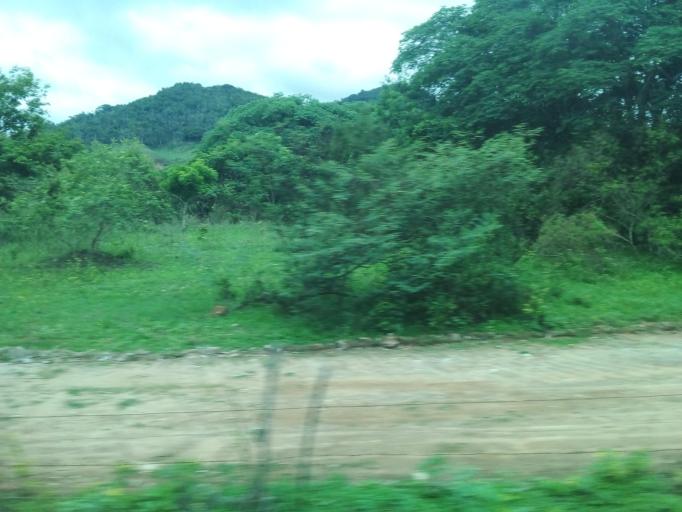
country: BR
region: Minas Gerais
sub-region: Nova Era
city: Nova Era
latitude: -19.7855
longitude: -43.0962
